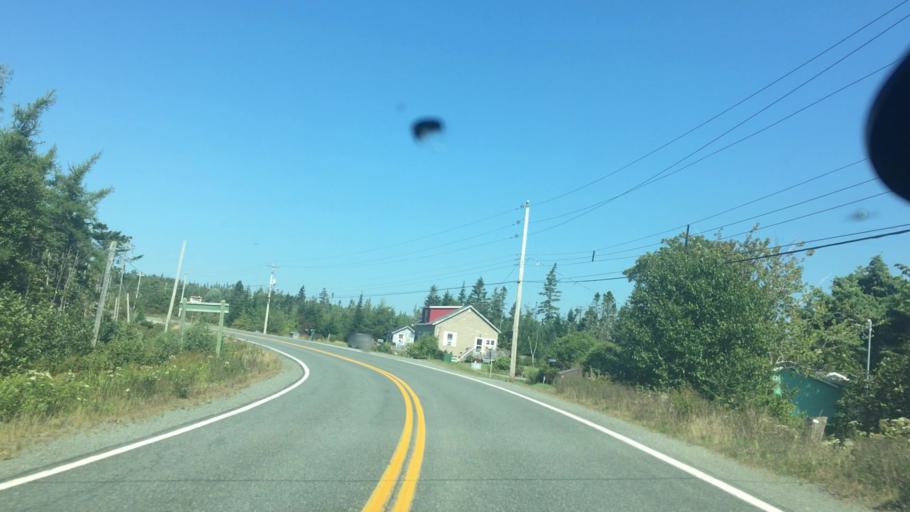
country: CA
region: Nova Scotia
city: Antigonish
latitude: 44.9999
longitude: -62.0995
